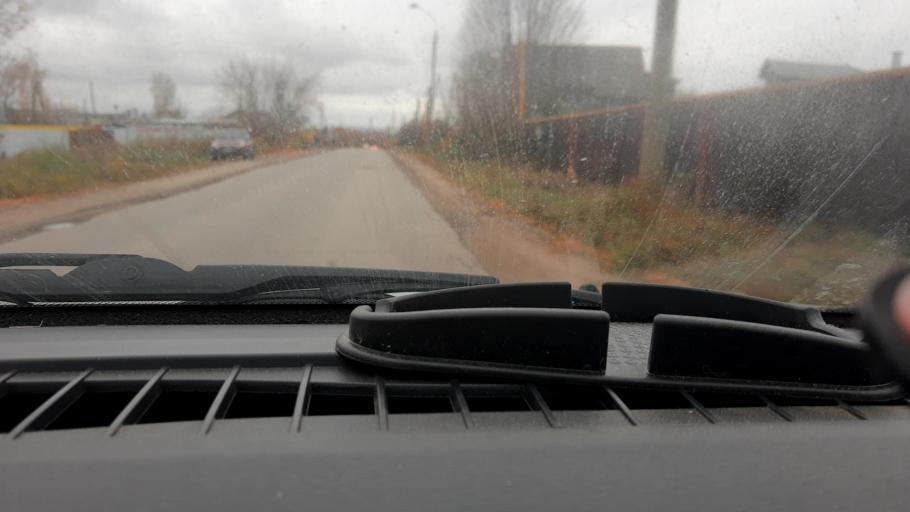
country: RU
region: Nizjnij Novgorod
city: Neklyudovo
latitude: 56.4078
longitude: 44.0162
